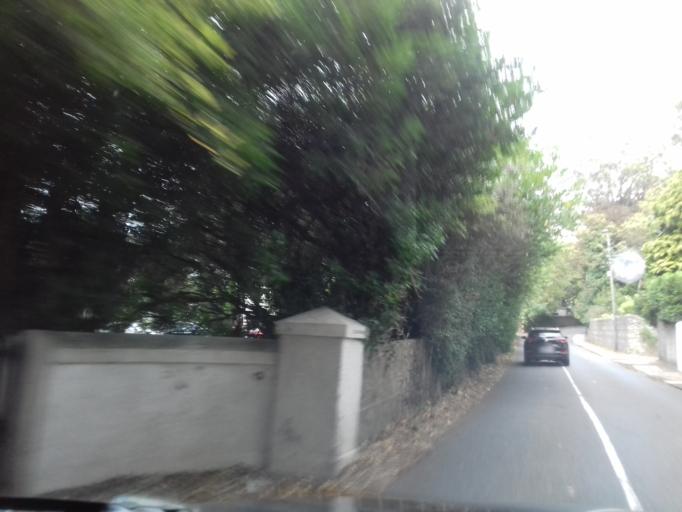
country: IE
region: Leinster
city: Loughlinstown
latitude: 53.2494
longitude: -6.1200
